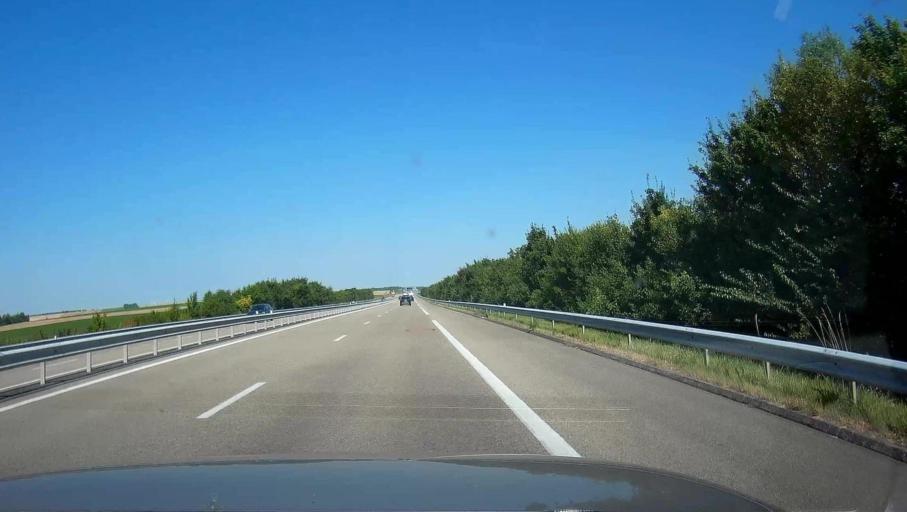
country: FR
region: Champagne-Ardenne
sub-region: Departement de l'Aube
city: Creney-pres-Troyes
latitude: 48.3839
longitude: 4.1558
